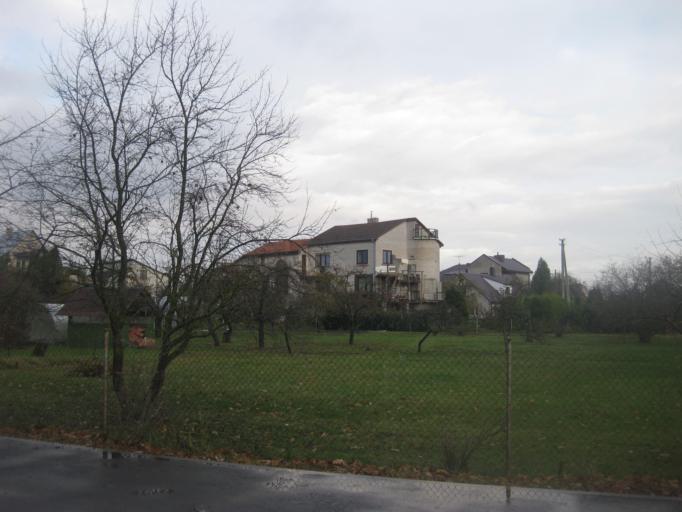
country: LT
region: Kauno apskritis
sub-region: Kaunas
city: Aleksotas
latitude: 54.8565
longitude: 23.8915
